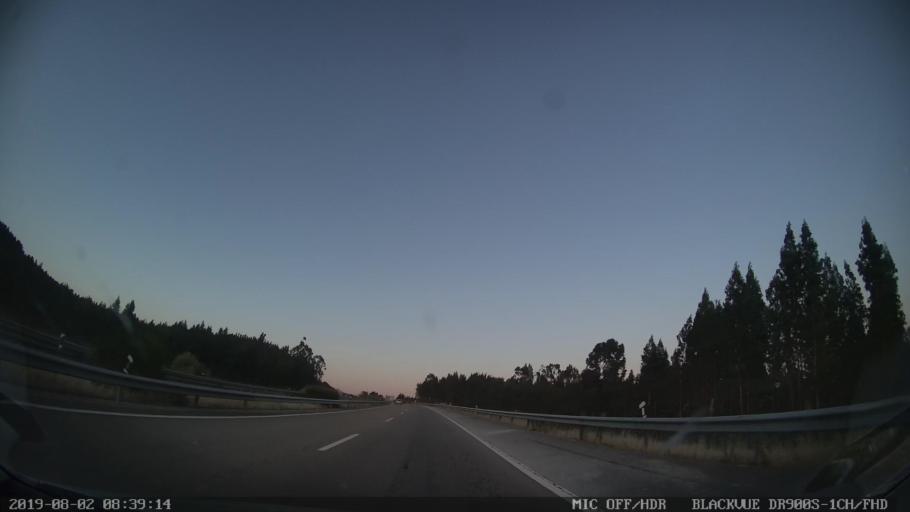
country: PT
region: Santarem
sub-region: Constancia
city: Constancia
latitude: 39.4889
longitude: -8.3163
